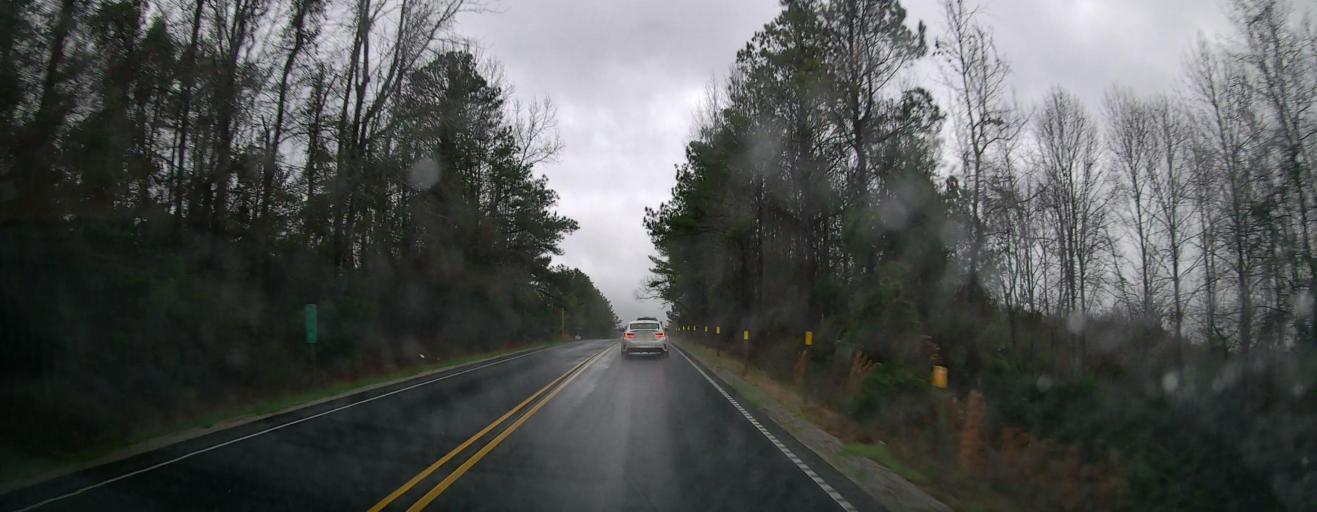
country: US
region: Alabama
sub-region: Chilton County
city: Clanton
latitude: 32.6236
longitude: -86.7371
